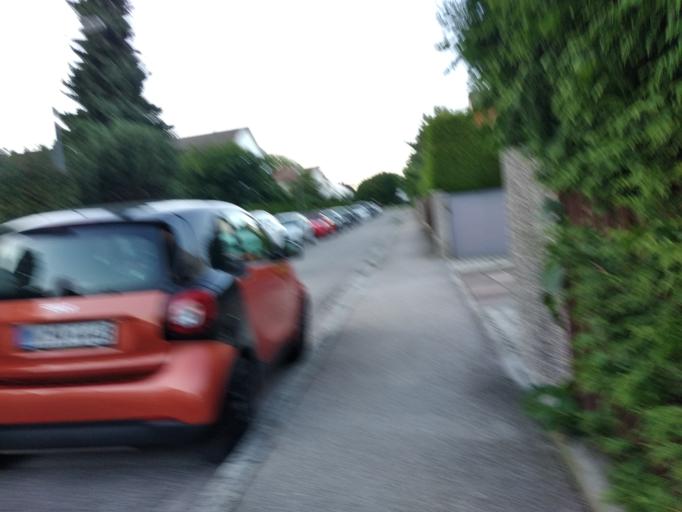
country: DE
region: Bavaria
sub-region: Upper Bavaria
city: Neubiberg
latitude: 48.1147
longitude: 11.6600
